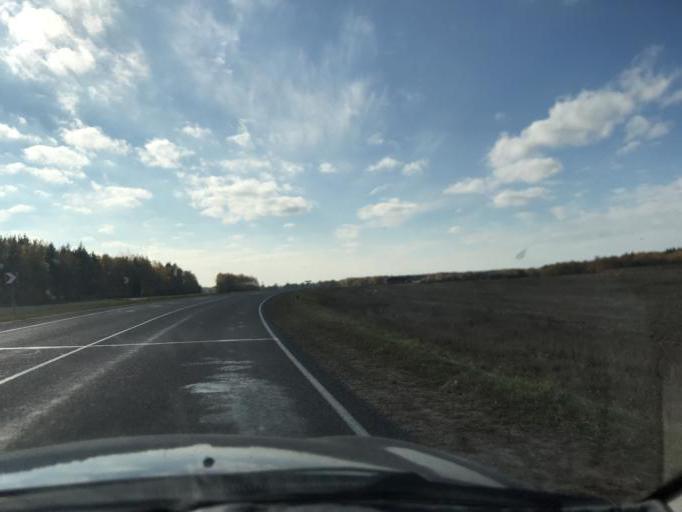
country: BY
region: Grodnenskaya
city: Voranava
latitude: 54.1918
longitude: 25.3445
